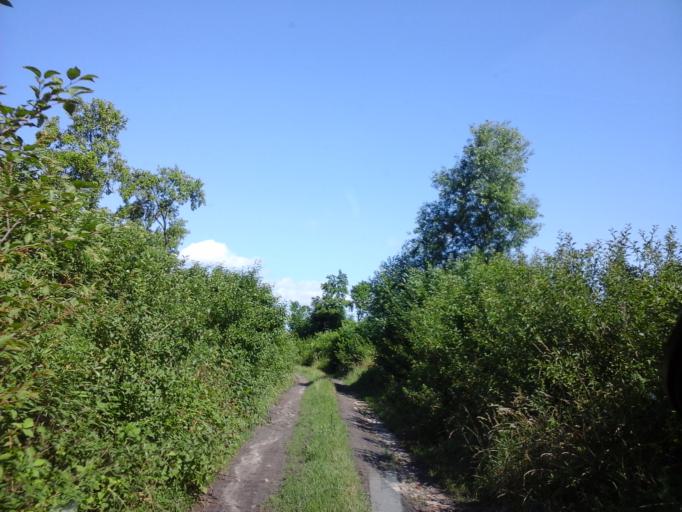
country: PL
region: West Pomeranian Voivodeship
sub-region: Powiat choszczenski
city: Recz
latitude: 53.1843
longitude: 15.5986
